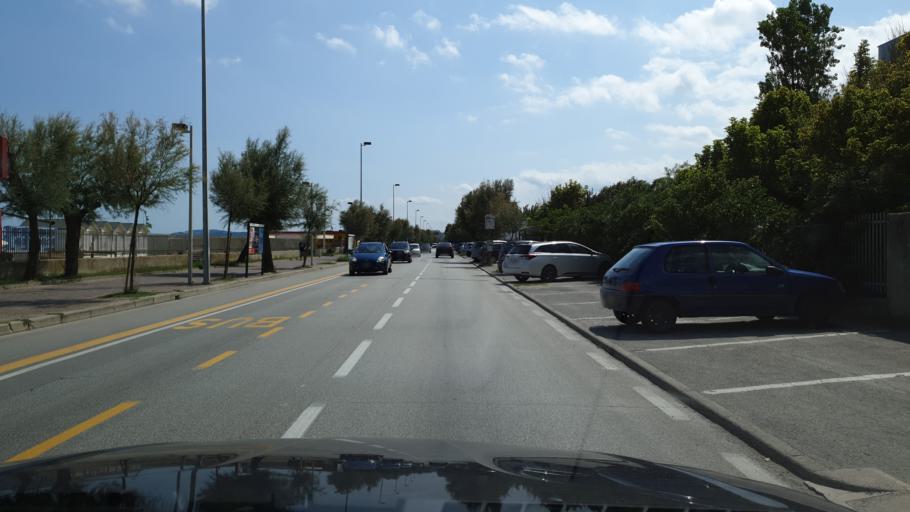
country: IT
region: Emilia-Romagna
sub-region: Provincia di Rimini
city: Misano Adriatico
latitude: 43.9876
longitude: 12.6852
